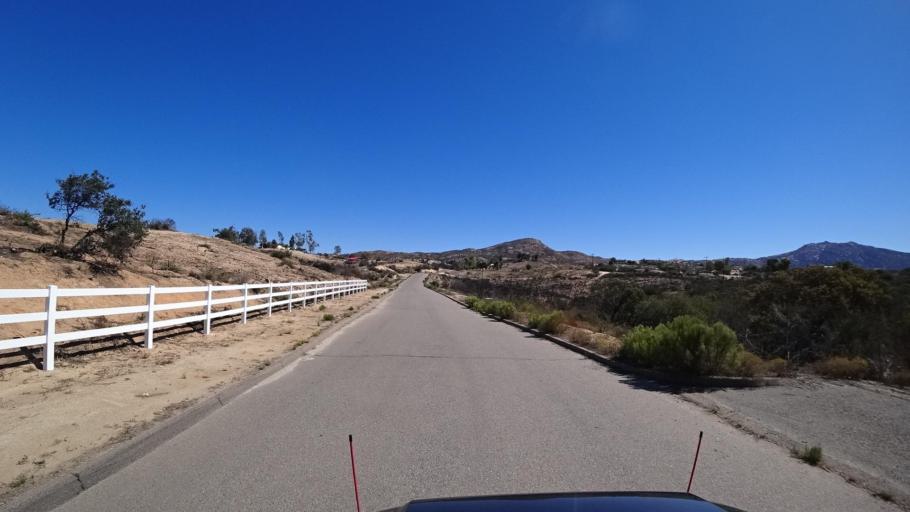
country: US
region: California
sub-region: San Diego County
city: Alpine
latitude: 32.7651
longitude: -116.7688
